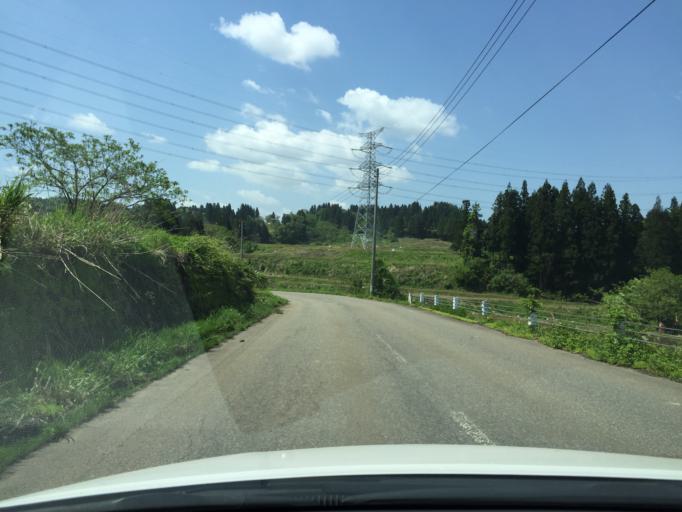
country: JP
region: Niigata
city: Tochio-honcho
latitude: 37.4844
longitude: 139.0490
